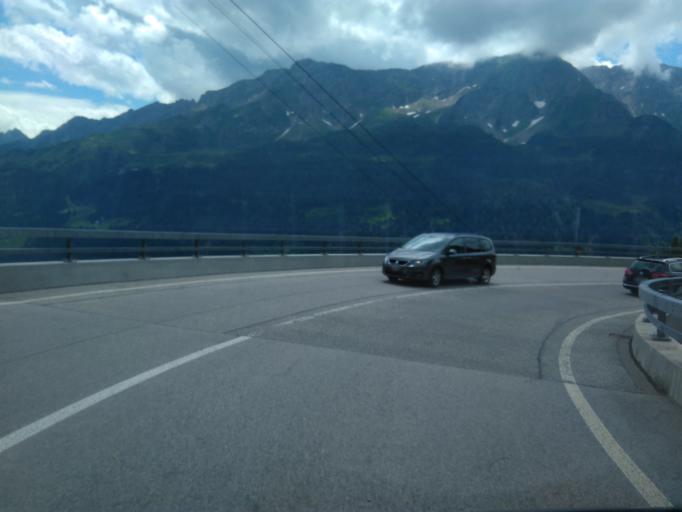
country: CH
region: Ticino
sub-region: Leventina District
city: Airolo
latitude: 46.5355
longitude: 8.5902
